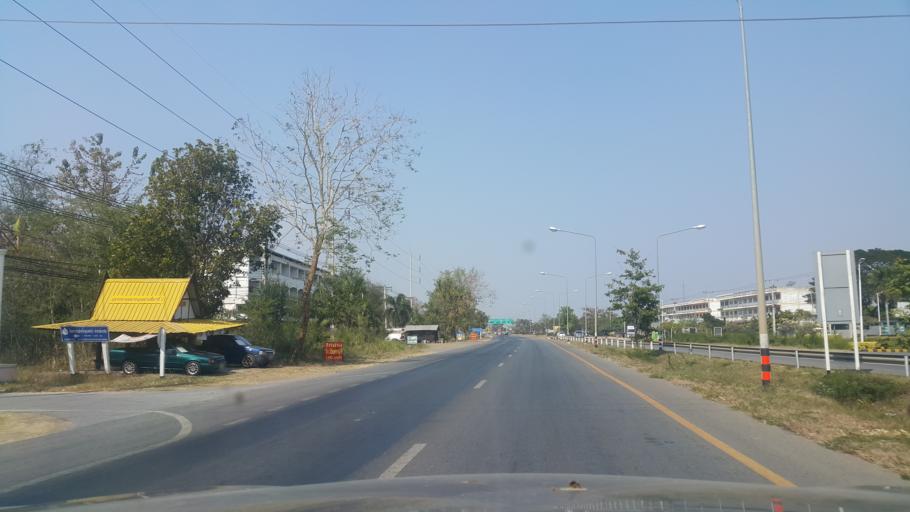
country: TH
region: Nakhon Ratchasima
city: Pak Thong Chai
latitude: 14.6887
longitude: 102.0179
